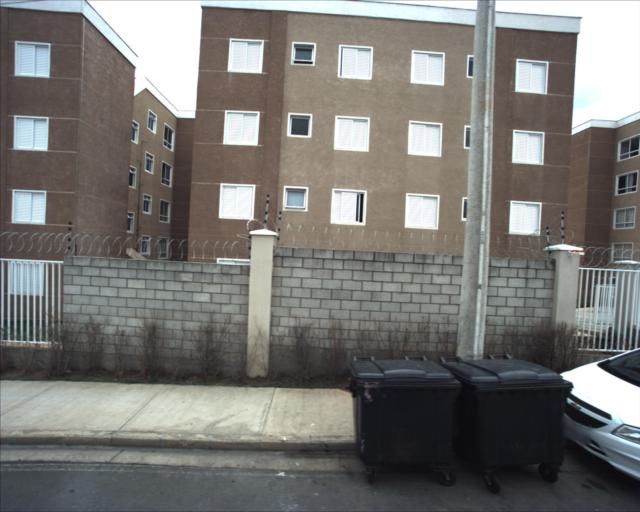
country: BR
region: Sao Paulo
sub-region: Sorocaba
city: Sorocaba
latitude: -23.4714
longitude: -47.4695
